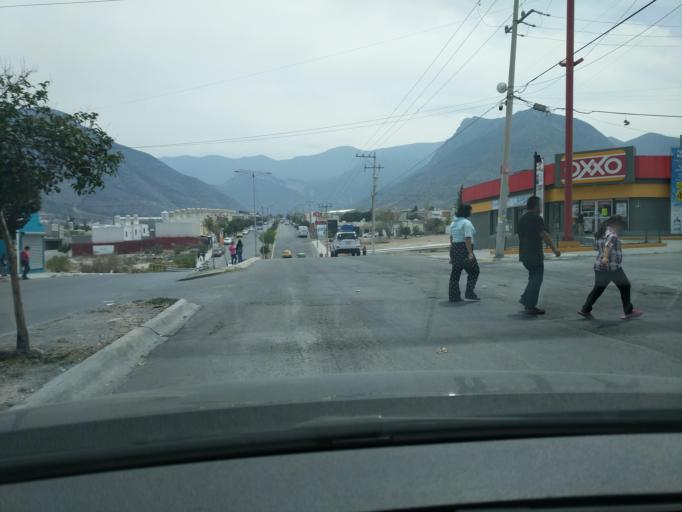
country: MX
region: Coahuila
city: Saltillo
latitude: 25.3541
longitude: -101.0155
